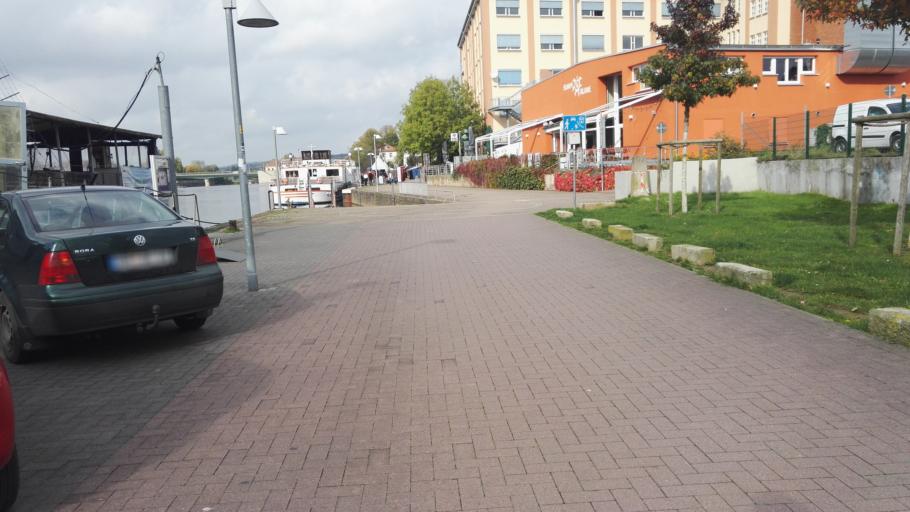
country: DE
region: Lower Saxony
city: Hameln
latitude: 52.0977
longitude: 9.3552
